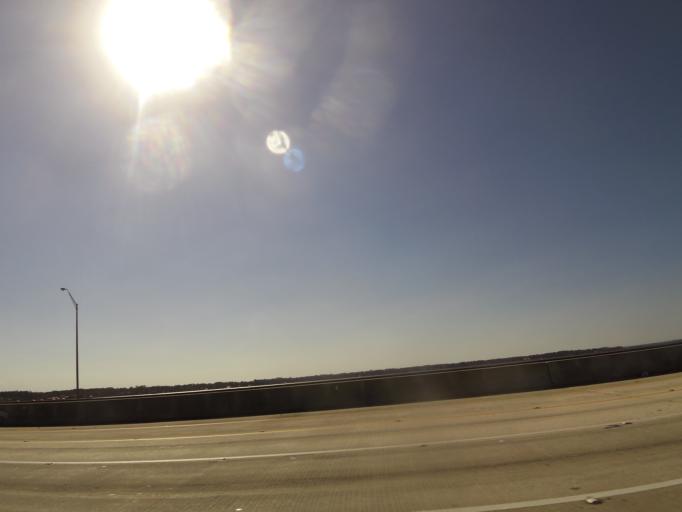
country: US
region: Florida
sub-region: Clay County
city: Orange Park
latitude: 30.1896
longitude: -81.6527
